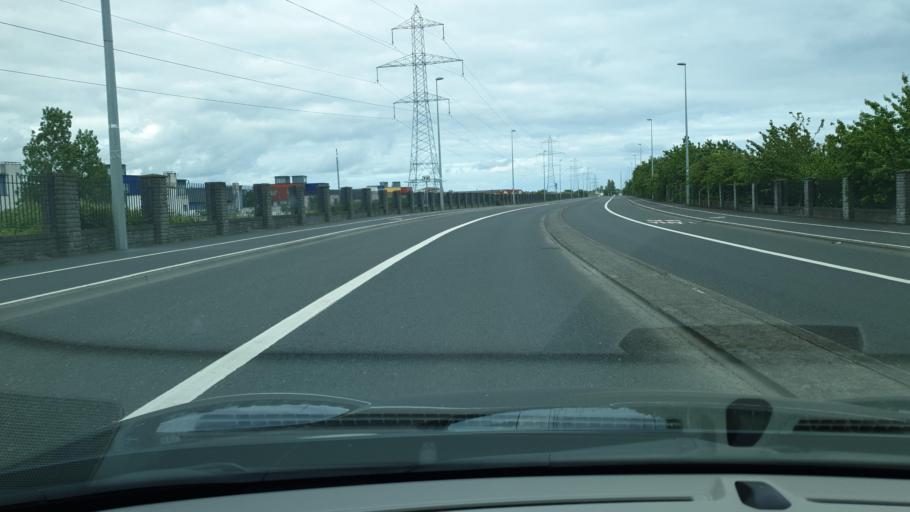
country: IE
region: Leinster
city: Clondalkin
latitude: 53.3374
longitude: -6.4206
